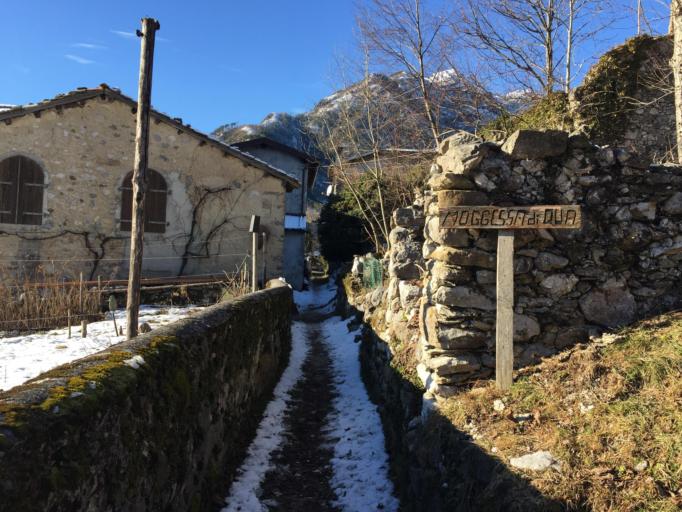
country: IT
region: Friuli Venezia Giulia
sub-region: Provincia di Udine
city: Moggio di Sotto
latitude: 46.4175
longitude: 13.1536
